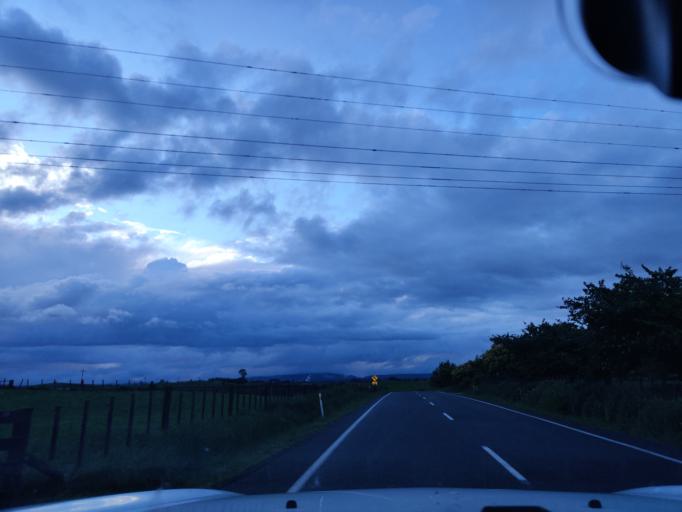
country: NZ
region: Waikato
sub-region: South Waikato District
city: Tokoroa
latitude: -38.2071
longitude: 175.8215
